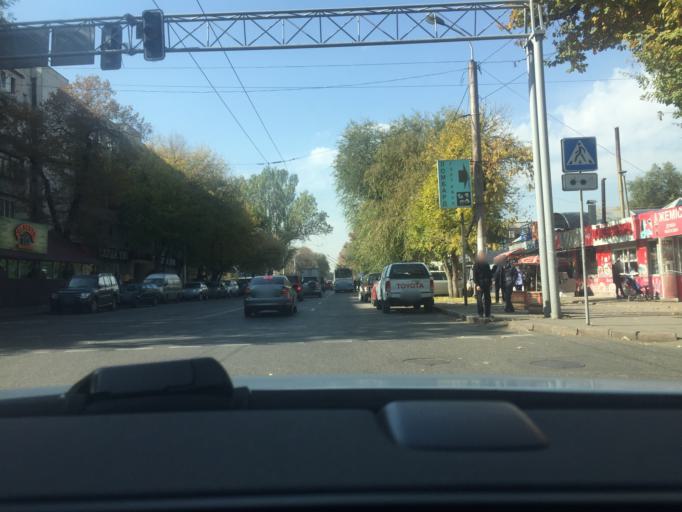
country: KZ
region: Almaty Qalasy
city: Almaty
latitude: 43.2581
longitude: 76.9183
